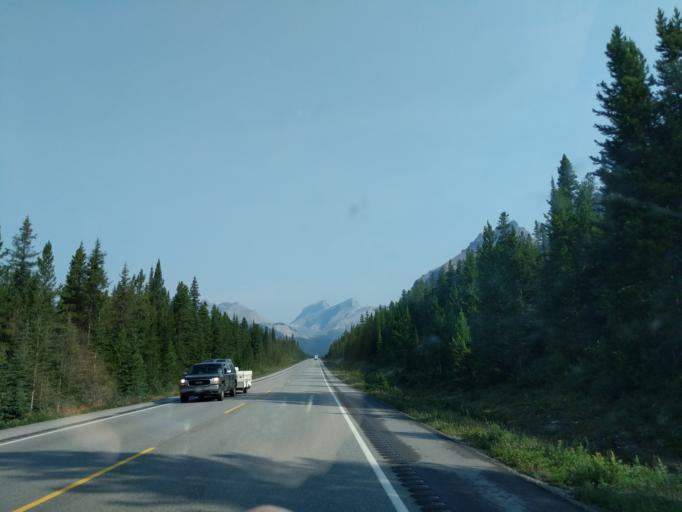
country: CA
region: Alberta
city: Lake Louise
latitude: 51.6044
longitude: -116.3107
